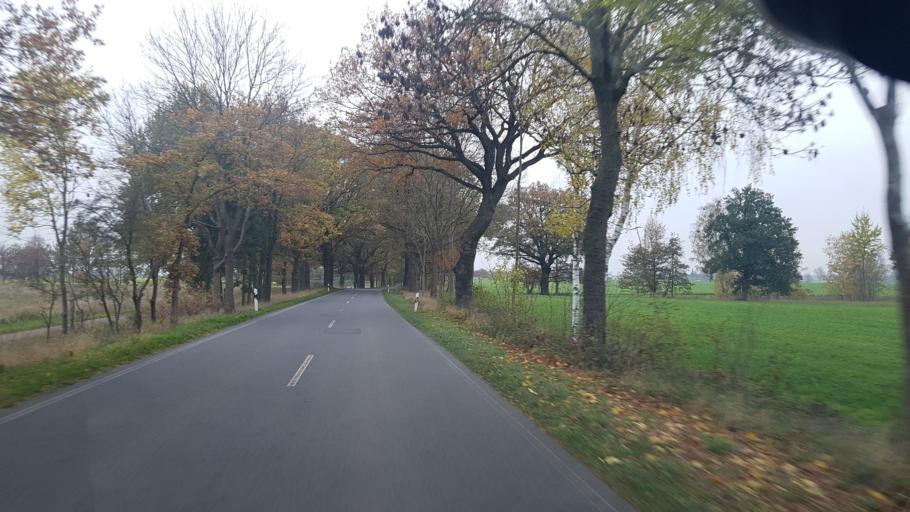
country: DE
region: Brandenburg
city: Schonermark
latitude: 52.9220
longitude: 13.1205
